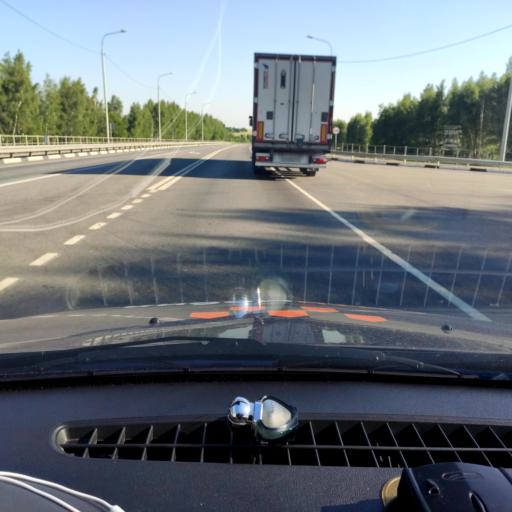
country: RU
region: Orjol
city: Zmiyevka
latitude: 52.7441
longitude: 36.3195
